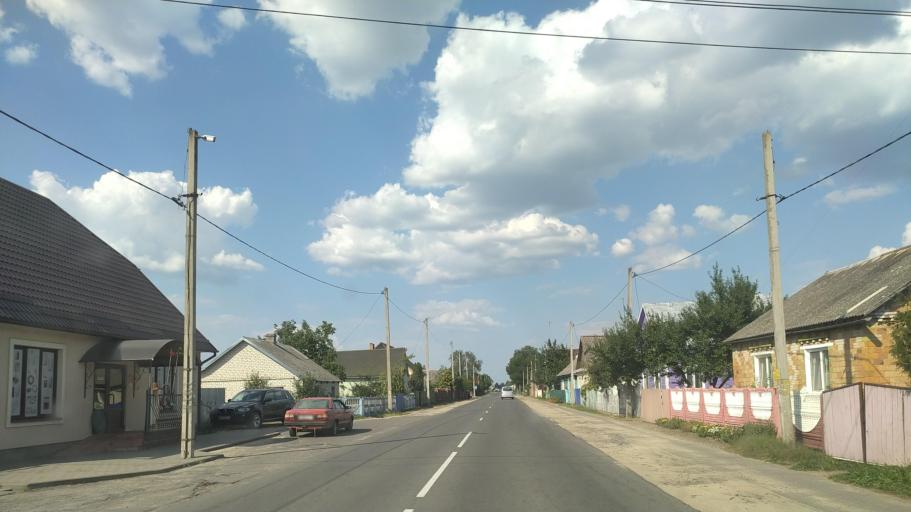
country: BY
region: Brest
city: Drahichyn
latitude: 52.1904
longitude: 25.1468
